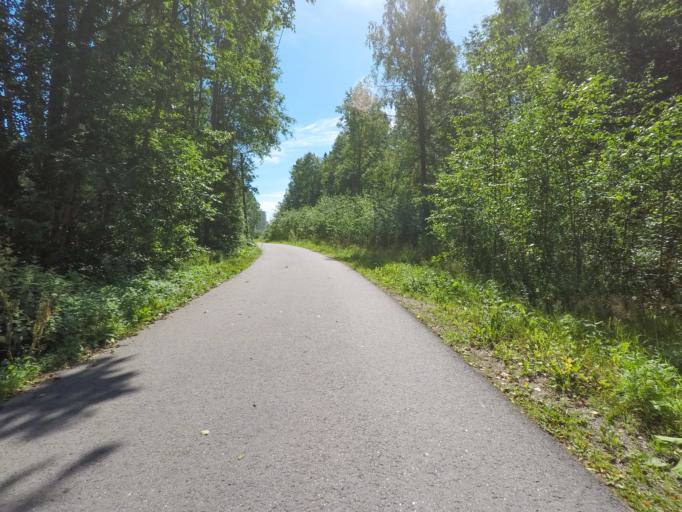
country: FI
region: Uusimaa
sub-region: Helsinki
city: Vantaa
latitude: 60.2157
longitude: 25.0703
